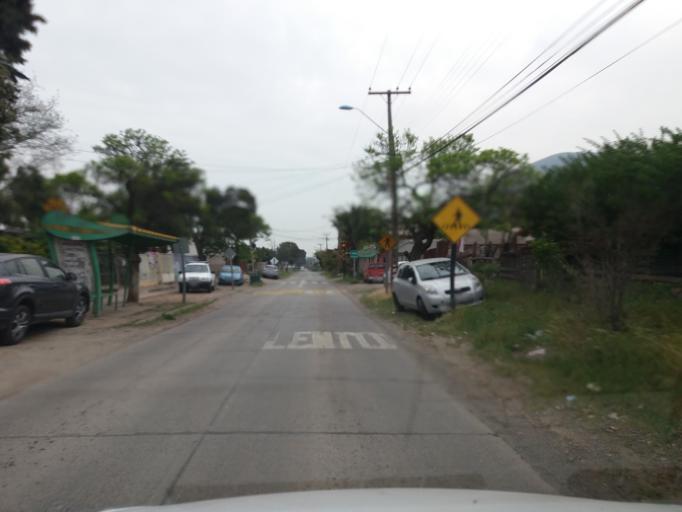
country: CL
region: Valparaiso
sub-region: Provincia de Quillota
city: Hacienda La Calera
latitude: -32.8343
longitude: -71.1145
